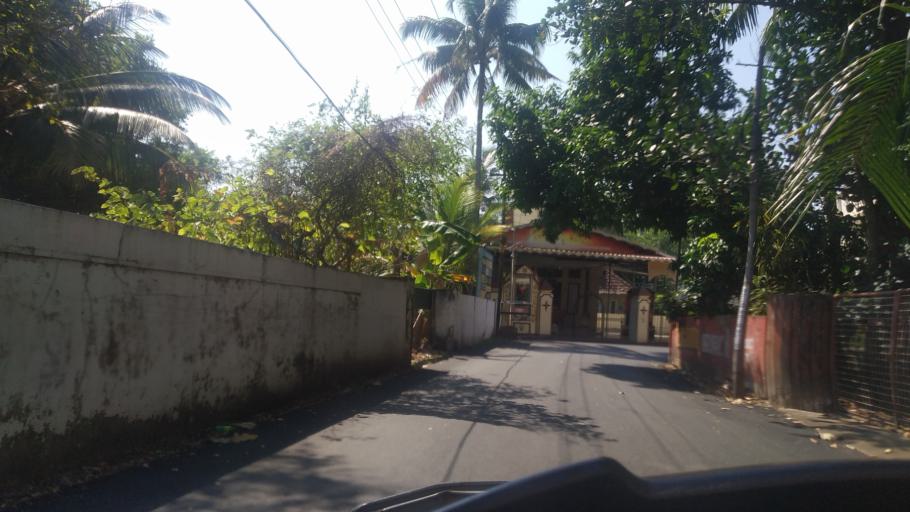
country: IN
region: Kerala
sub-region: Ernakulam
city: Elur
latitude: 10.0421
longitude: 76.2232
